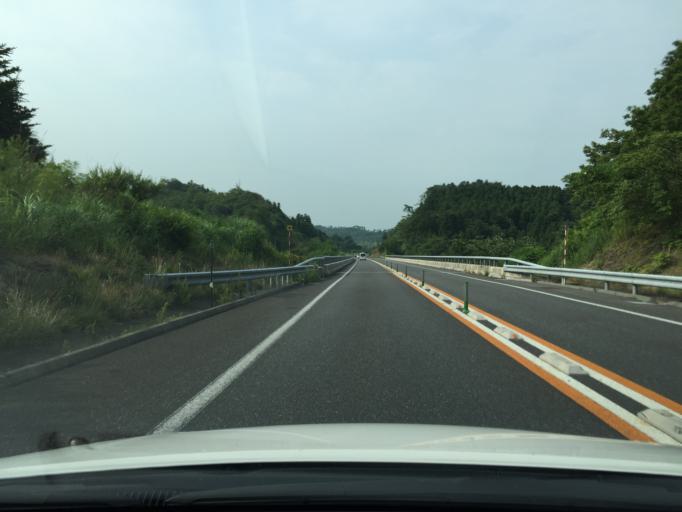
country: JP
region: Fukushima
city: Iwaki
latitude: 37.1589
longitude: 140.9665
